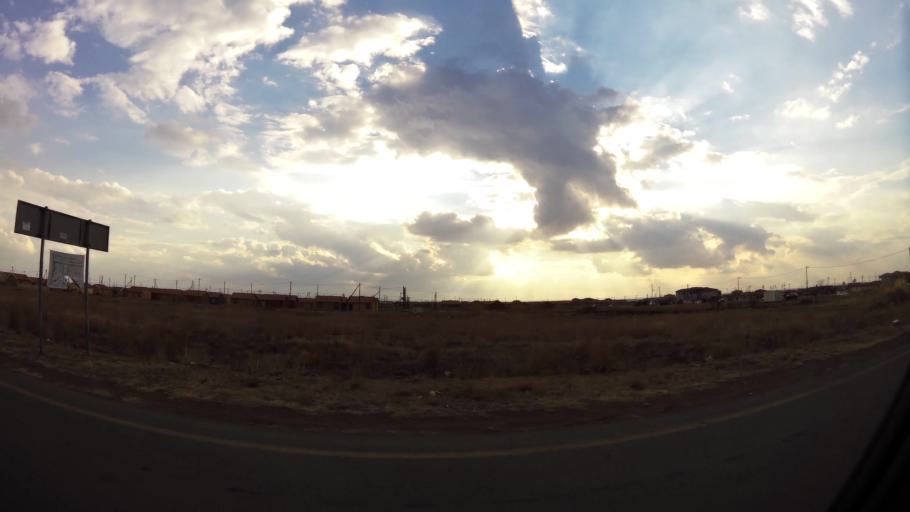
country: ZA
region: Gauteng
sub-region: Sedibeng District Municipality
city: Vanderbijlpark
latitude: -26.6149
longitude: 27.8138
